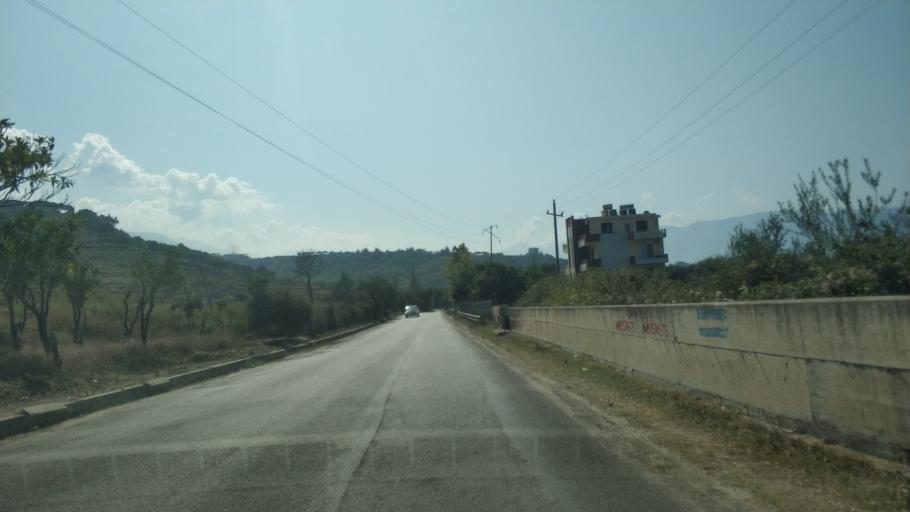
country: AL
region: Vlore
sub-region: Rrethi i Vlores
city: Orikum
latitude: 40.3751
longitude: 19.4823
